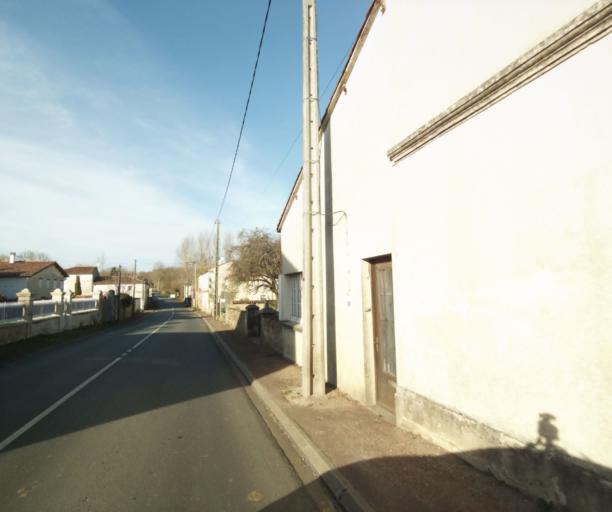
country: FR
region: Poitou-Charentes
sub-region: Departement de la Charente-Maritime
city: Burie
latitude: 45.7892
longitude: -0.4357
